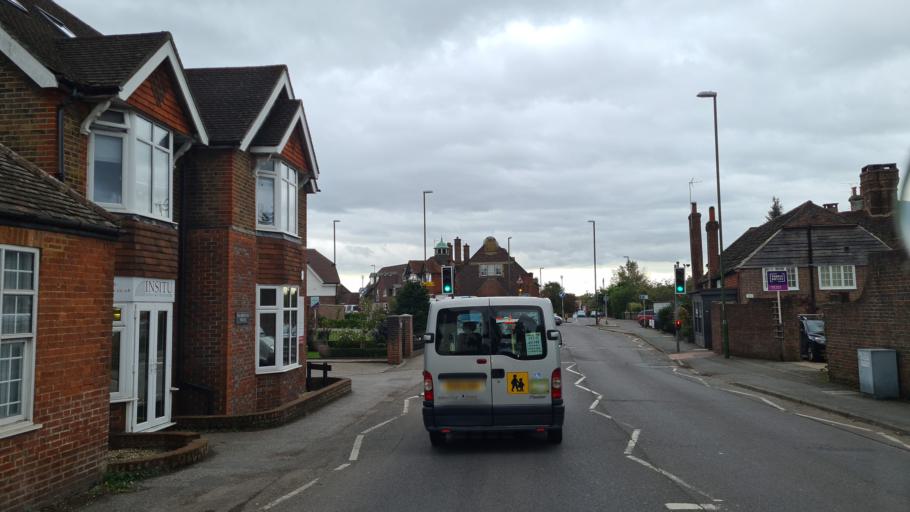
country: GB
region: England
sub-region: West Sussex
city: Partridge Green
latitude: 50.9904
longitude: -0.2726
